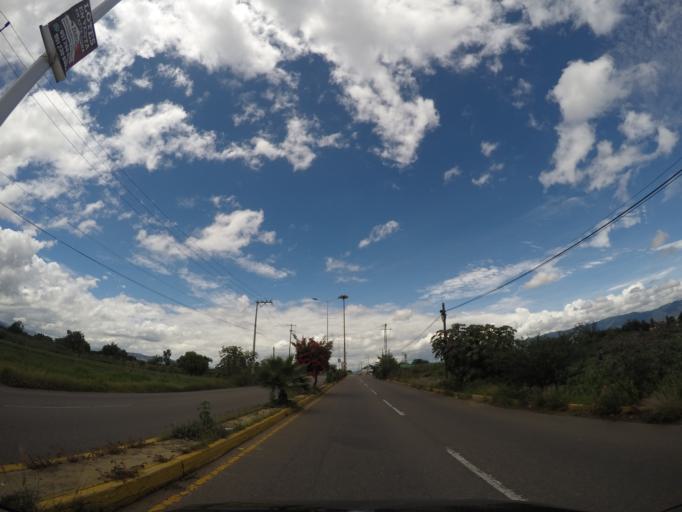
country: MX
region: Oaxaca
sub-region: Santa Cruz Xoxocotlan
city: San Isidro Monjas
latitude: 16.9979
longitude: -96.7413
